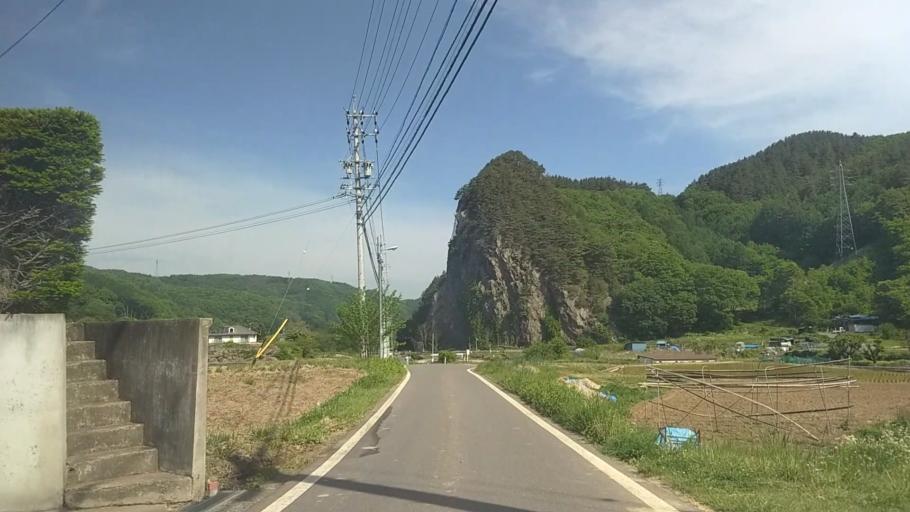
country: JP
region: Nagano
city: Saku
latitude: 36.1074
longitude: 138.4833
